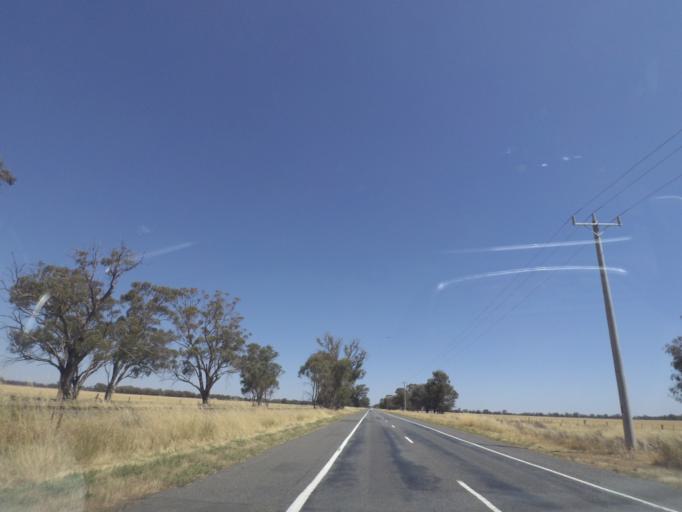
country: AU
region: Victoria
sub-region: Greater Shepparton
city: Shepparton
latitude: -36.2016
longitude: 145.4318
